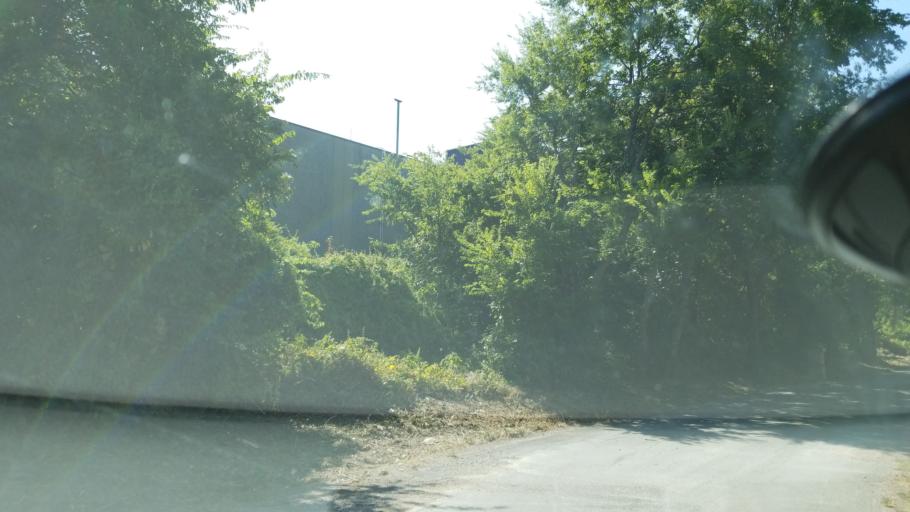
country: US
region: Texas
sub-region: Dallas County
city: Cockrell Hill
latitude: 32.7014
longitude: -96.9196
